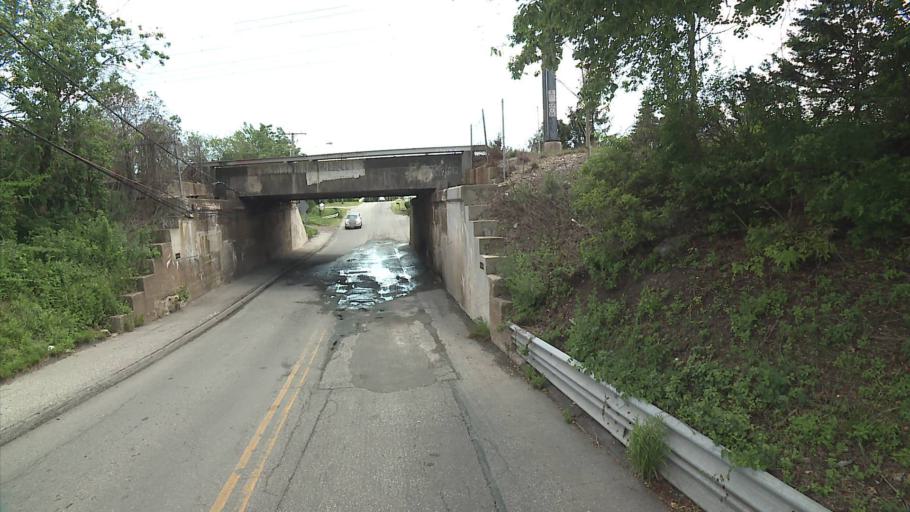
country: US
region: Connecticut
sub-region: New London County
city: Poquonock Bridge
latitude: 41.3422
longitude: -72.0390
